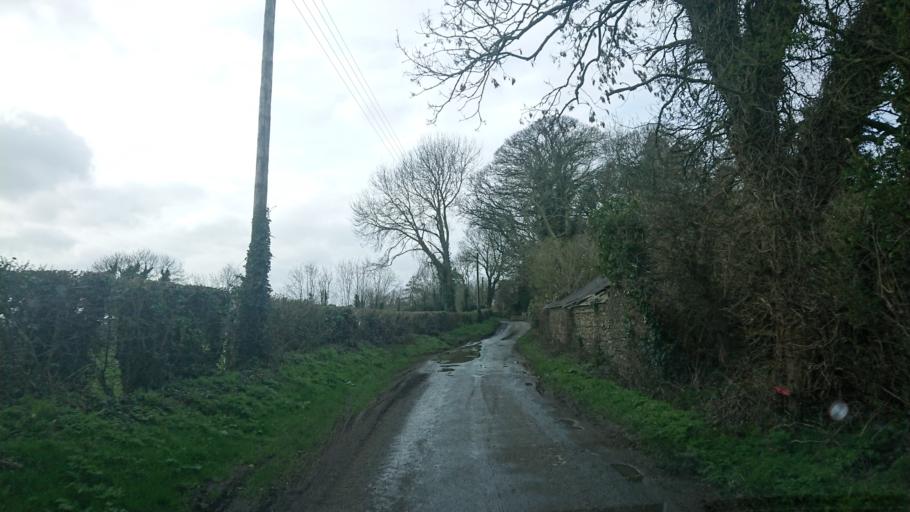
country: IE
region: Leinster
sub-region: Kildare
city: Eadestown
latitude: 53.1726
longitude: -6.6245
